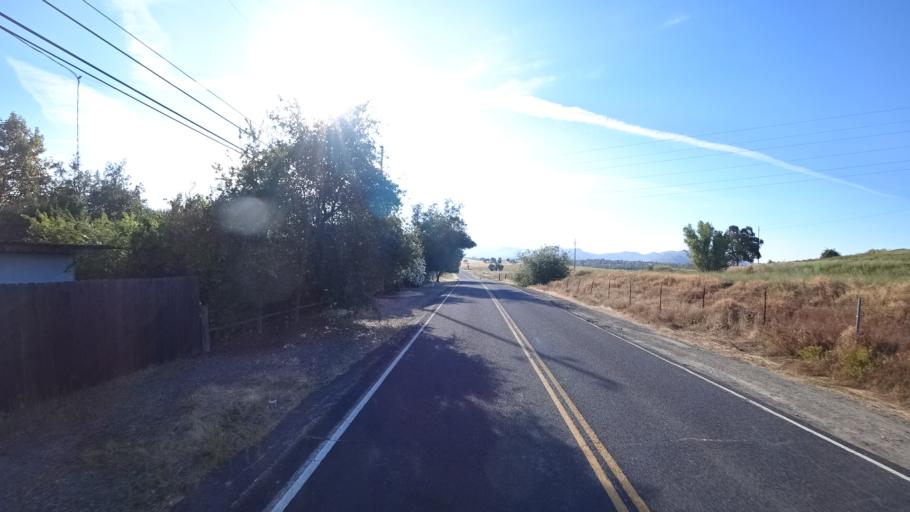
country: US
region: California
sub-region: Calaveras County
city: Valley Springs
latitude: 38.1929
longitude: -120.8182
